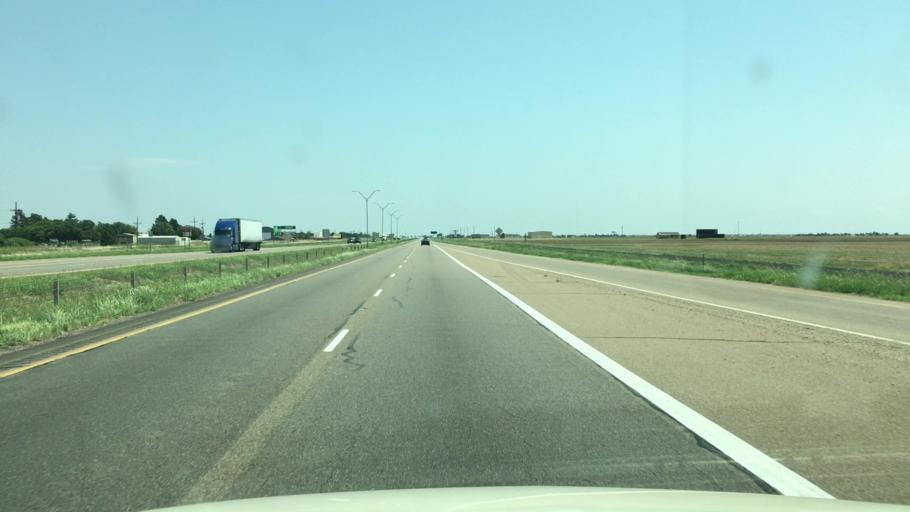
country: US
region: Texas
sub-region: Potter County
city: Bushland
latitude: 35.1899
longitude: -102.0060
